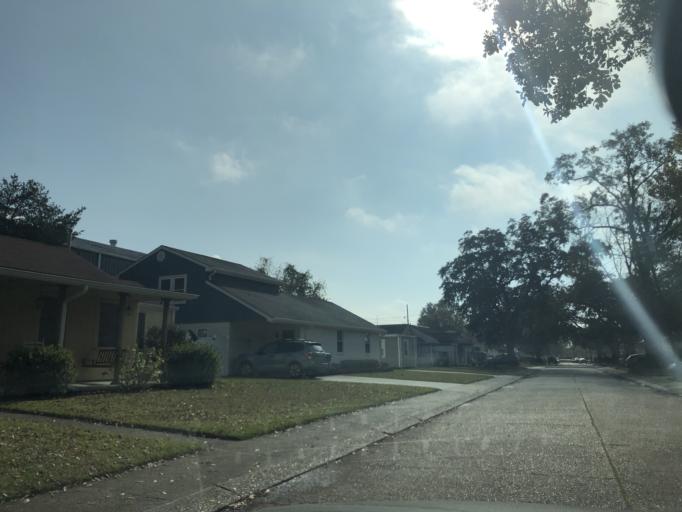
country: US
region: Louisiana
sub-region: Jefferson Parish
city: Metairie Terrace
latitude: 29.9738
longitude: -90.1659
